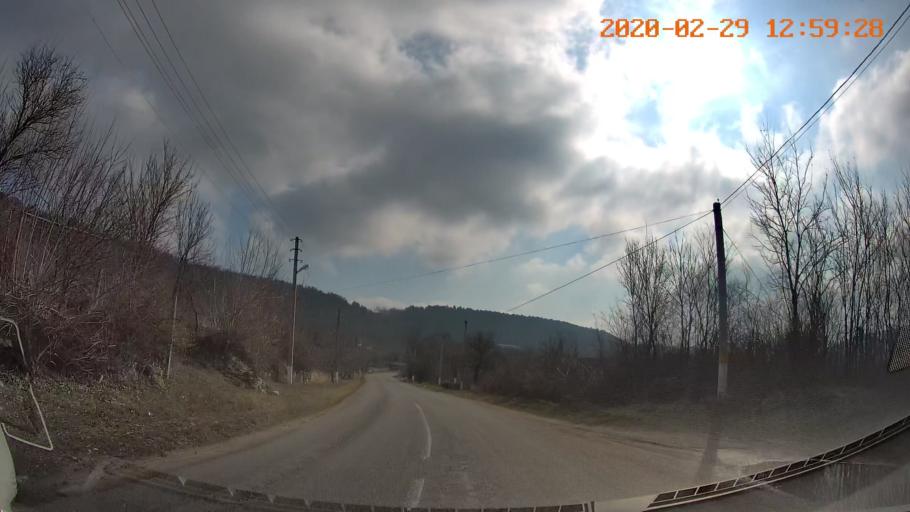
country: MD
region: Telenesti
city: Camenca
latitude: 48.0618
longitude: 28.7241
